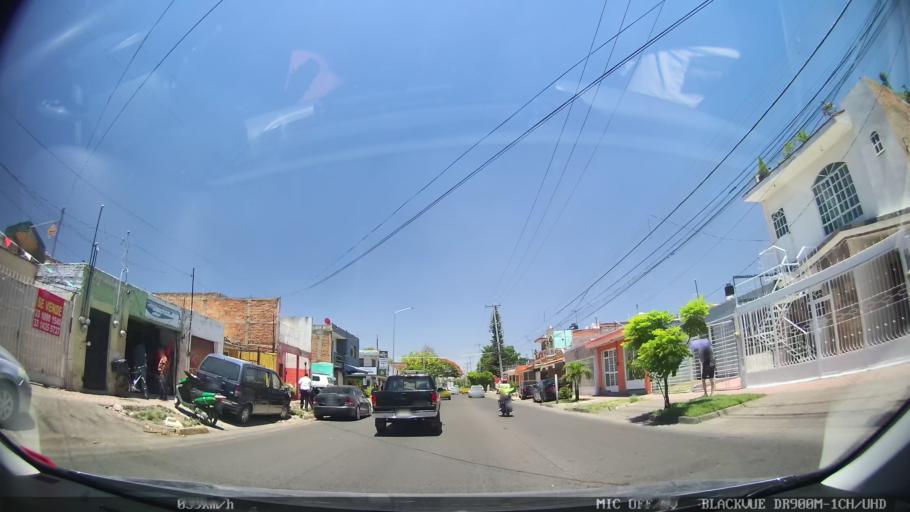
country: MX
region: Jalisco
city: Tlaquepaque
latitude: 20.6616
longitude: -103.2922
